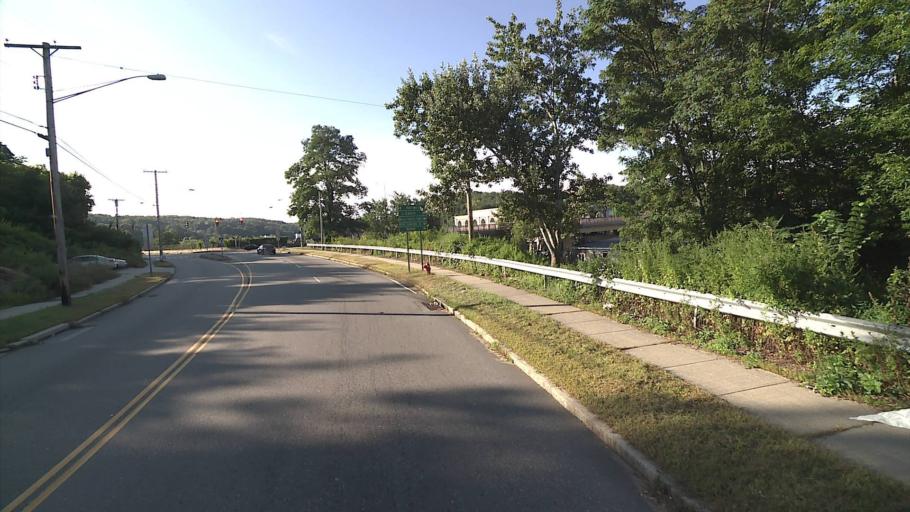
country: US
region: Connecticut
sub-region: New London County
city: Norwich
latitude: 41.5262
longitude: -72.0820
